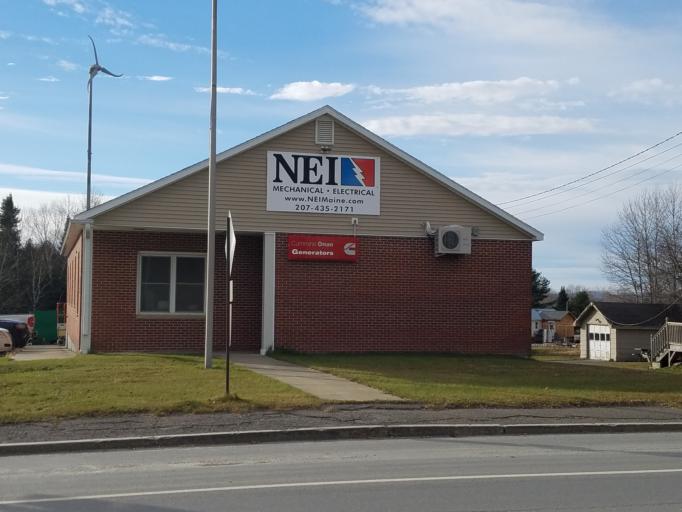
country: US
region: Maine
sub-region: Aroostook County
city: Presque Isle
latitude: 46.6269
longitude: -68.4022
